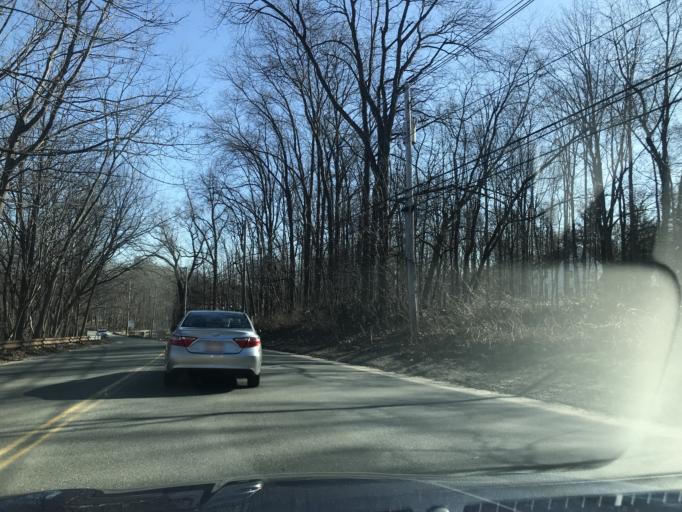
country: US
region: Massachusetts
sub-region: Essex County
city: North Andover
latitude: 42.7070
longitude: -71.0715
